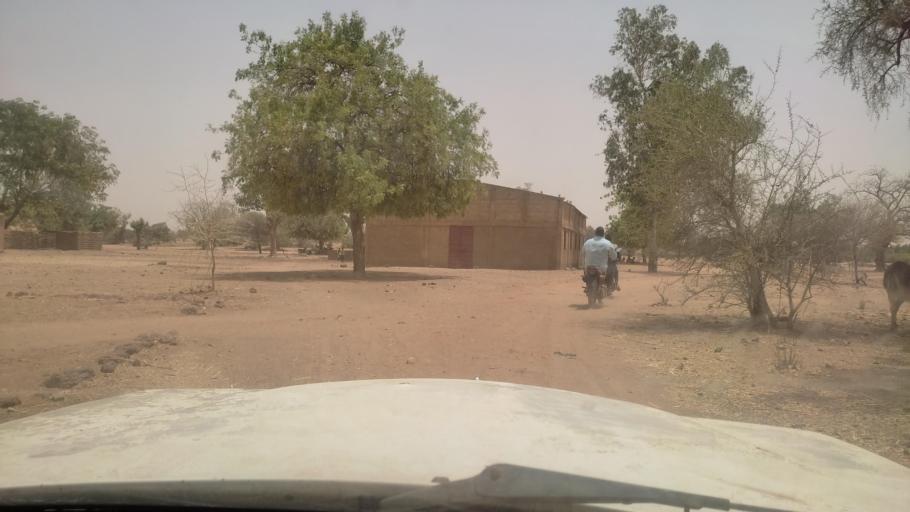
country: BF
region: Est
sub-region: Gnagna Province
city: Bogande
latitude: 13.0078
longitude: -0.0896
